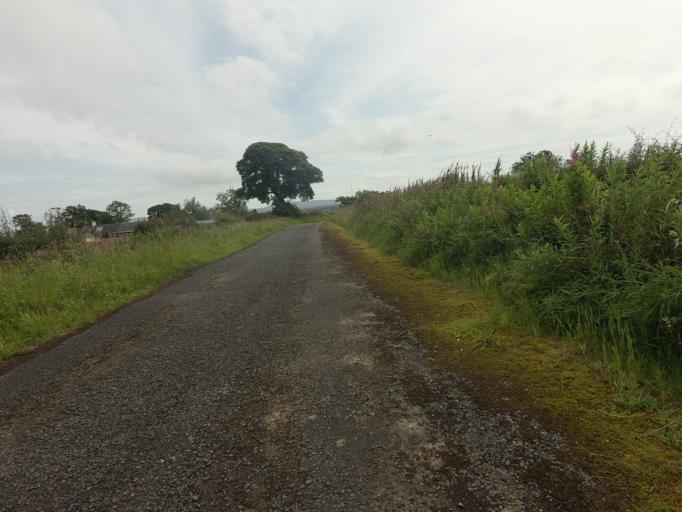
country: GB
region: Scotland
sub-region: West Lothian
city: West Calder
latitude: 55.8863
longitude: -3.5690
